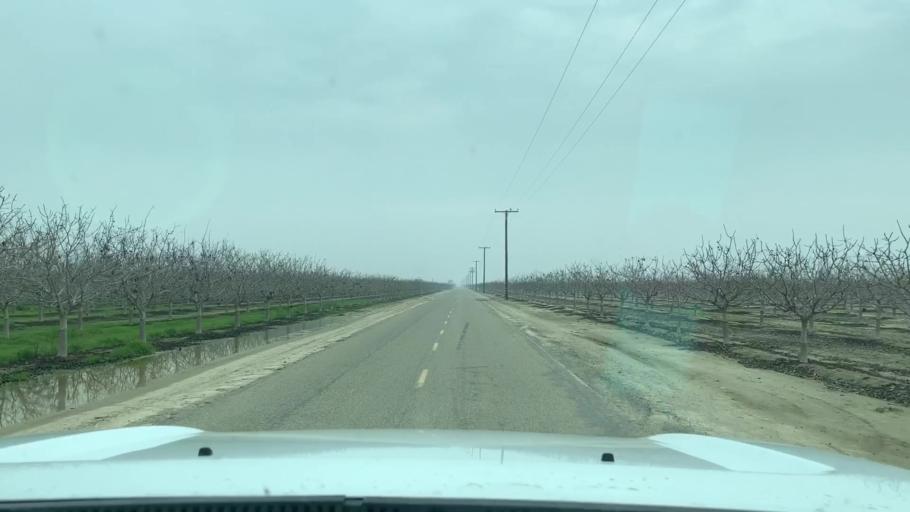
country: US
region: California
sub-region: Tulare County
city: Earlimart
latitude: 35.8193
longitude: -119.3484
